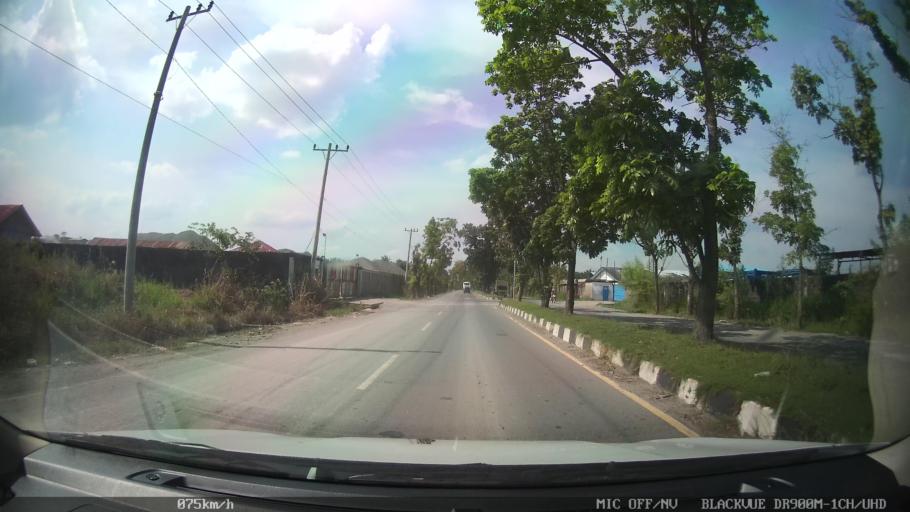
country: ID
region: North Sumatra
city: Binjai
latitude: 3.6327
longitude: 98.5351
